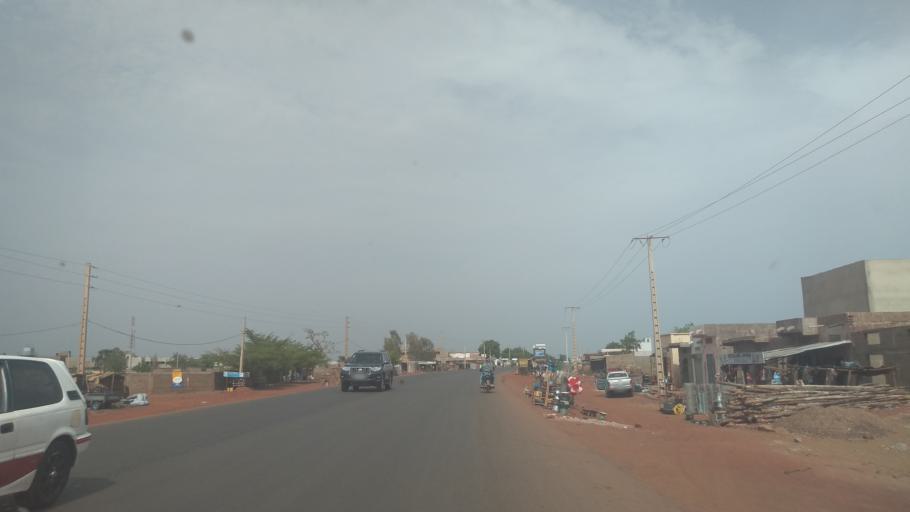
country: ML
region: Bamako
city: Bamako
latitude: 12.5871
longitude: -7.8323
